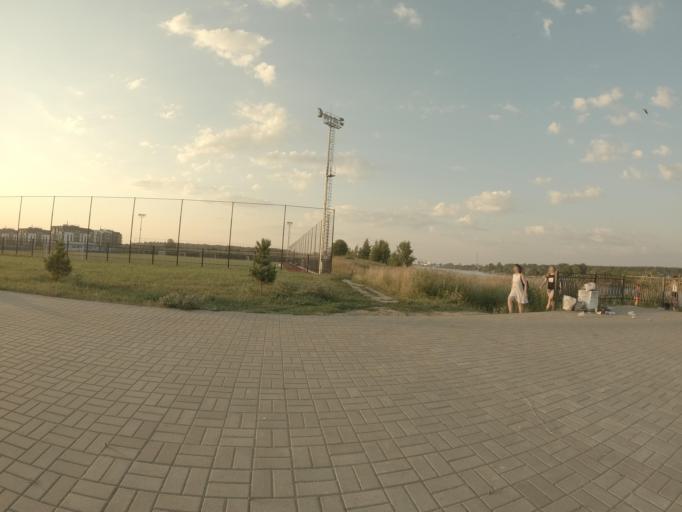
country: RU
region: Leningrad
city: Pavlovo
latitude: 59.8476
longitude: 30.9436
